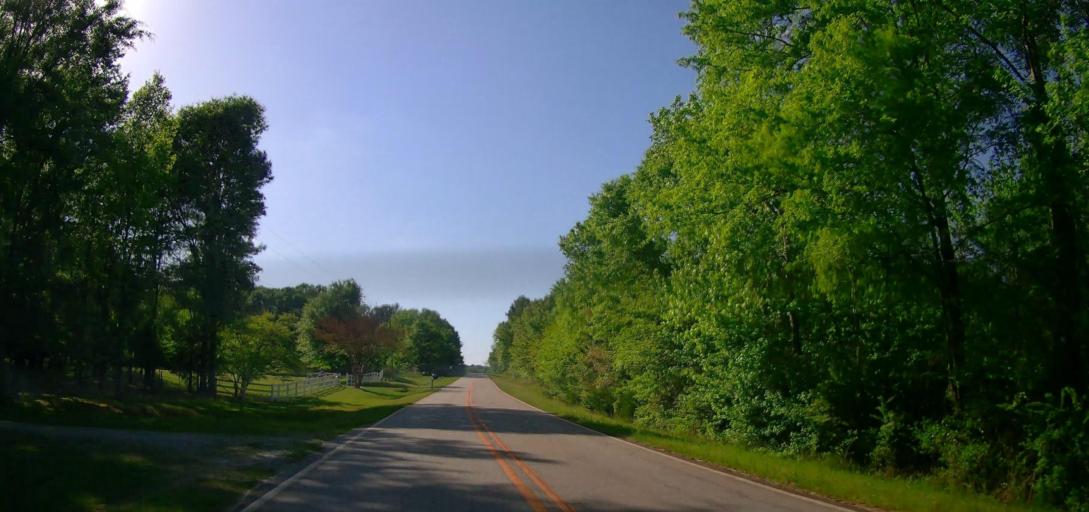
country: US
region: Georgia
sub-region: Morgan County
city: Madison
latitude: 33.5166
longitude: -83.5014
